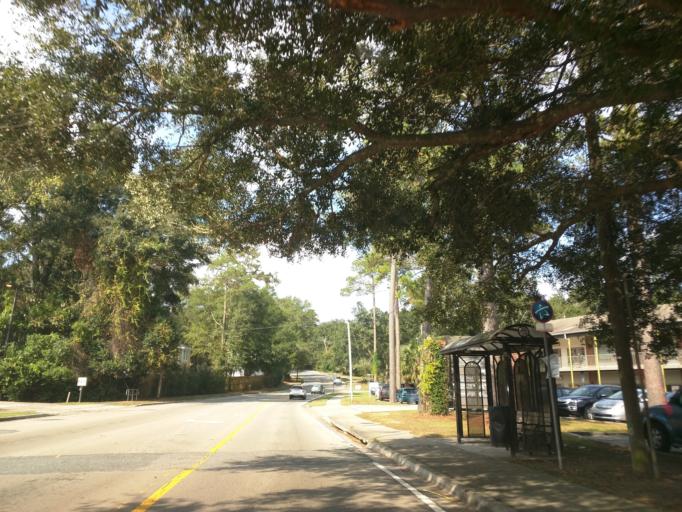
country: US
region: Florida
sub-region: Leon County
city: Tallahassee
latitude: 30.4668
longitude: -84.2691
